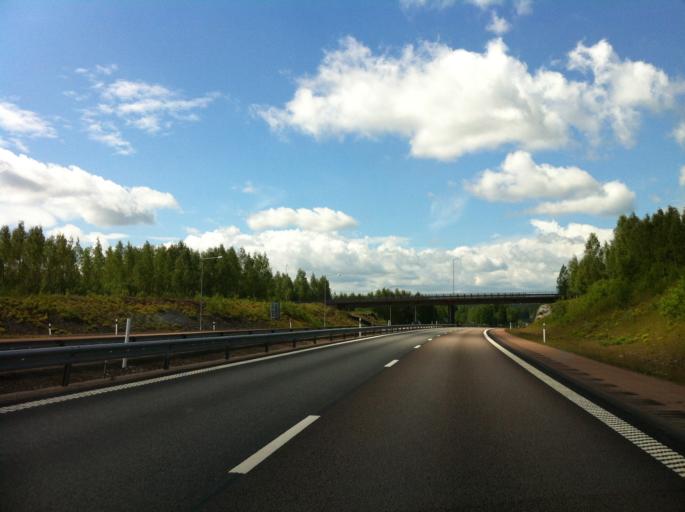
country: SE
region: Vaermland
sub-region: Grums Kommun
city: Slottsbron
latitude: 59.2860
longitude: 13.0449
